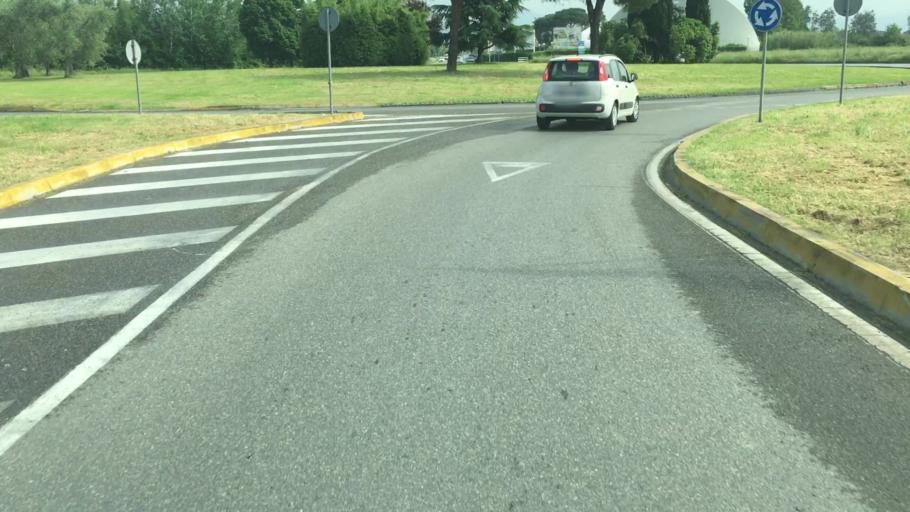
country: IT
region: Tuscany
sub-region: Province of Florence
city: Campi Bisenzio
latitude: 43.8153
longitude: 11.1205
